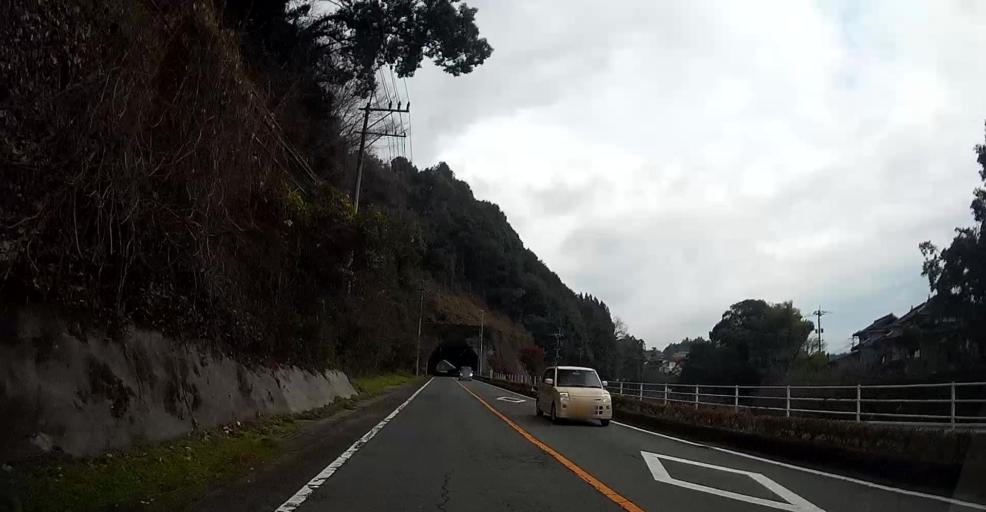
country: JP
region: Kumamoto
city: Matsubase
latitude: 32.6166
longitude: 130.8537
